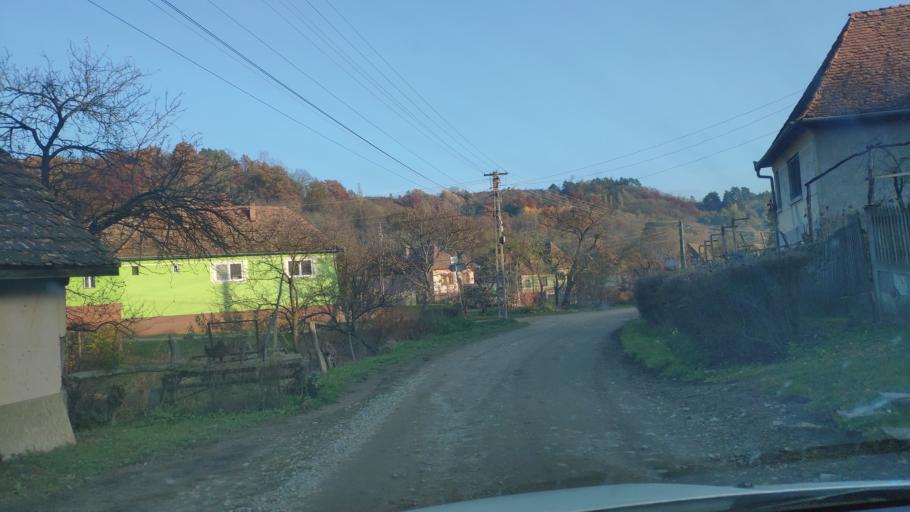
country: RO
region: Mures
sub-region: Comuna Ghindari
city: Ghindari
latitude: 46.5272
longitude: 24.9127
